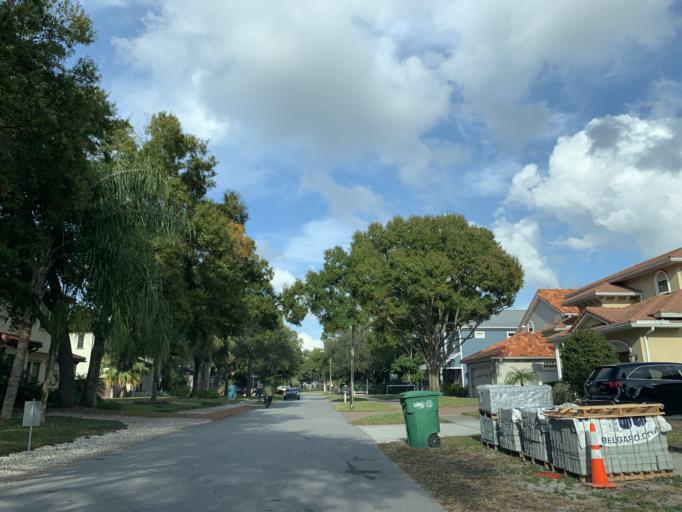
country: US
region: Florida
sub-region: Hillsborough County
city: Tampa
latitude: 27.9054
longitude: -82.5002
